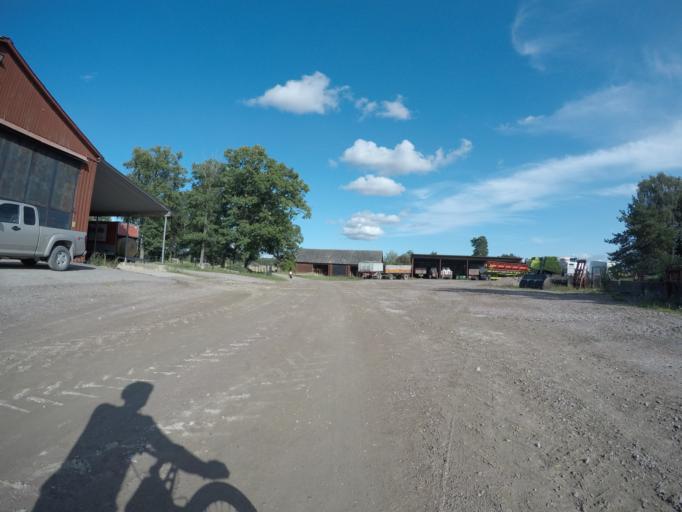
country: SE
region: Soedermanland
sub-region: Eskilstuna Kommun
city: Kvicksund
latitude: 59.5122
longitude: 16.3543
